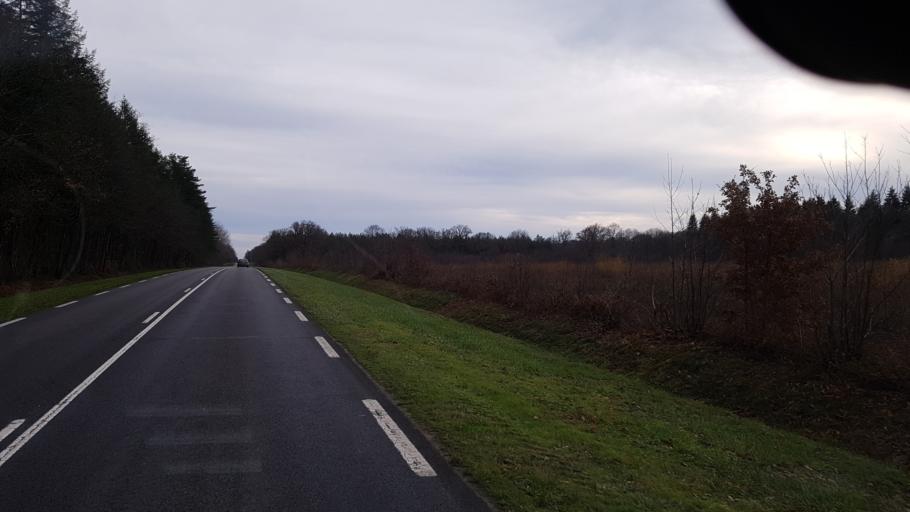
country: FR
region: Centre
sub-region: Departement du Loir-et-Cher
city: Lamotte-Beuvron
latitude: 47.6277
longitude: 2.0073
